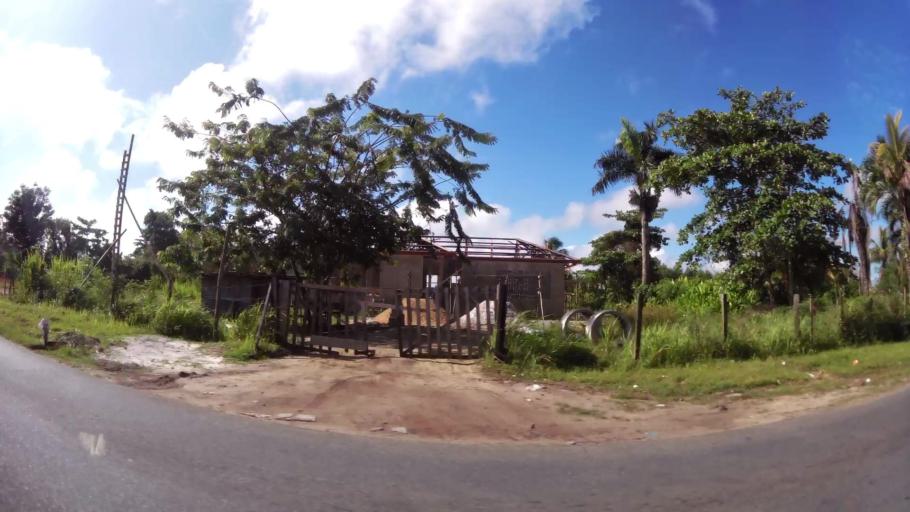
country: SR
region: Paramaribo
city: Paramaribo
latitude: 5.8356
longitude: -55.1275
